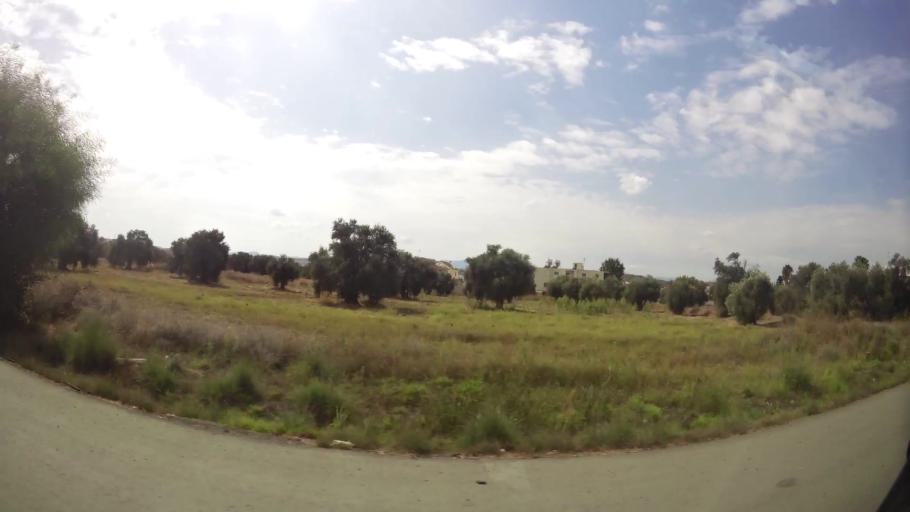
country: CY
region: Lefkosia
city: Tseri
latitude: 35.0685
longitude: 33.3306
